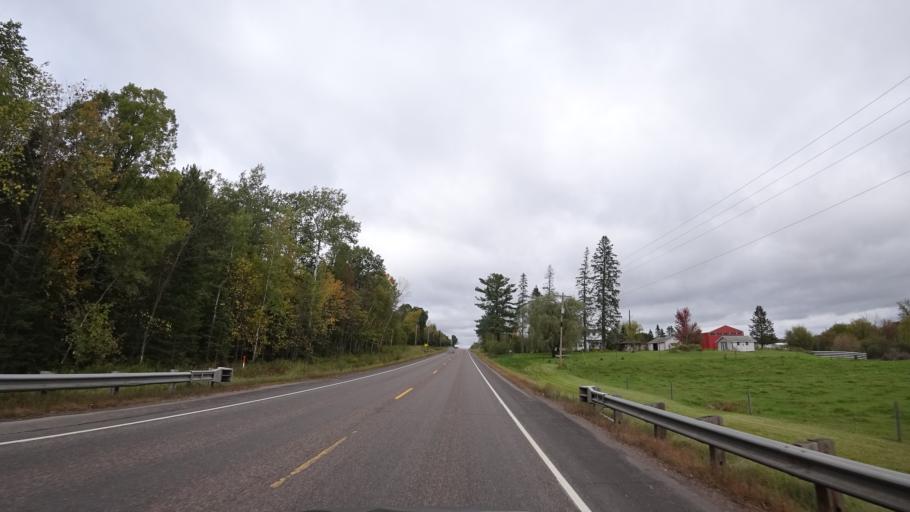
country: US
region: Wisconsin
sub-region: Rusk County
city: Ladysmith
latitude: 45.4299
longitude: -91.1107
